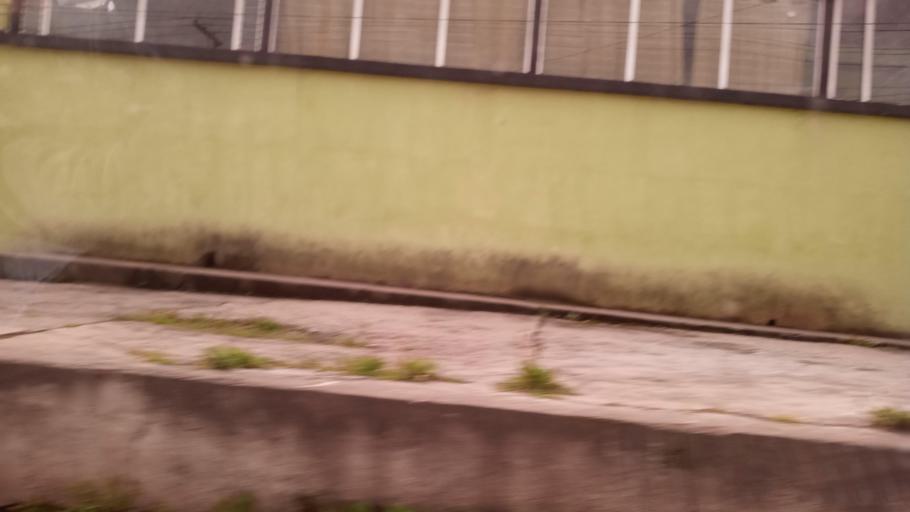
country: GT
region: Quetzaltenango
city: Quetzaltenango
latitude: 14.8301
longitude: -91.5240
